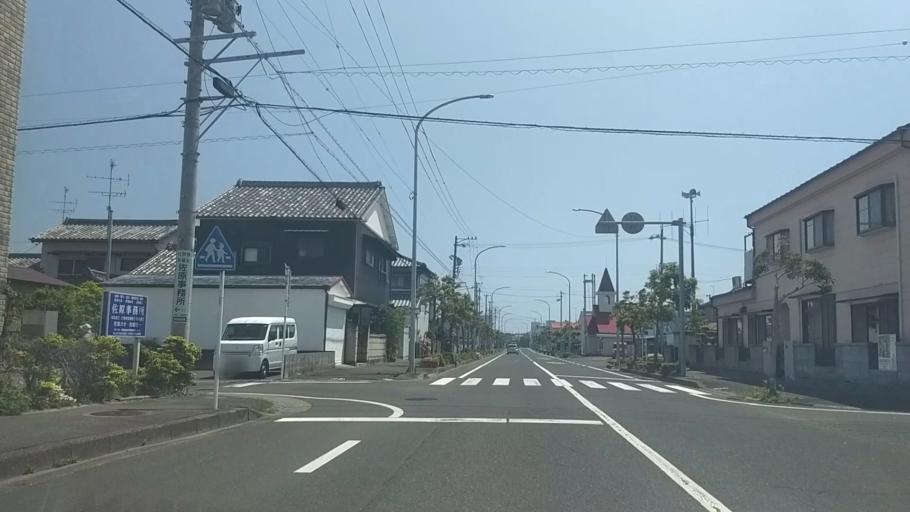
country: JP
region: Shizuoka
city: Kosai-shi
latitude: 34.6885
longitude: 137.5696
